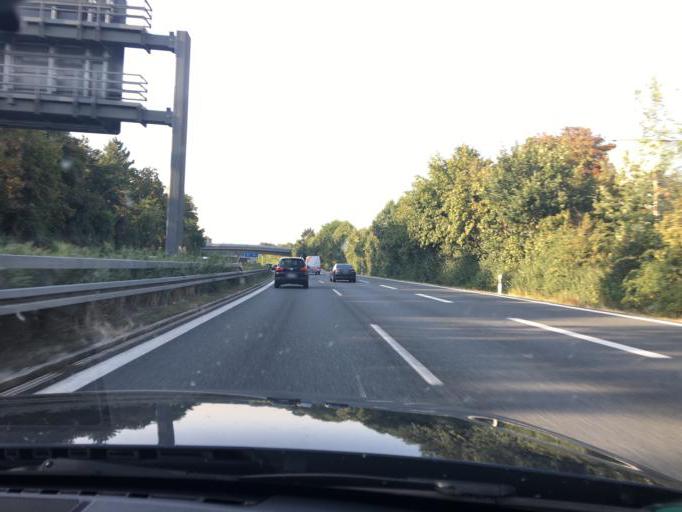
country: DE
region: Bavaria
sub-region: Regierungsbezirk Mittelfranken
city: Erlangen
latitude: 49.5703
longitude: 10.9908
